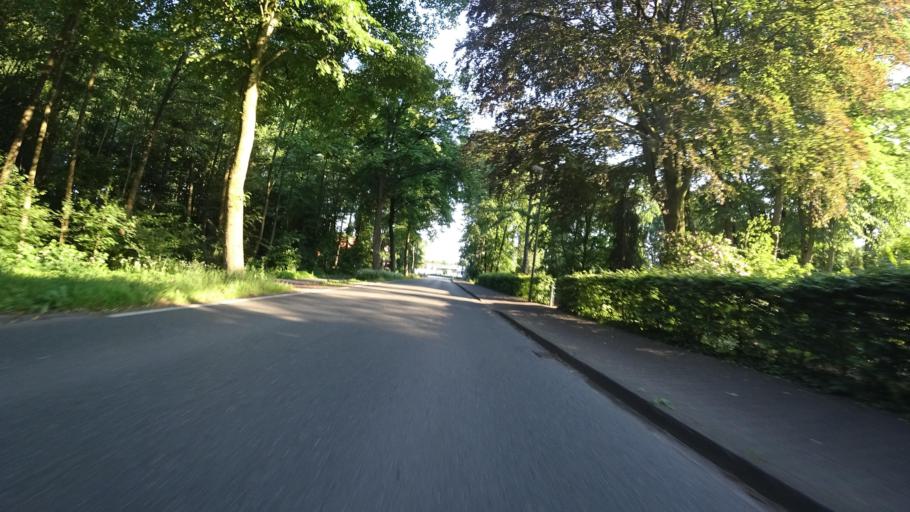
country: DE
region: North Rhine-Westphalia
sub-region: Regierungsbezirk Detmold
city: Guetersloh
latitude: 51.9443
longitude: 8.4123
